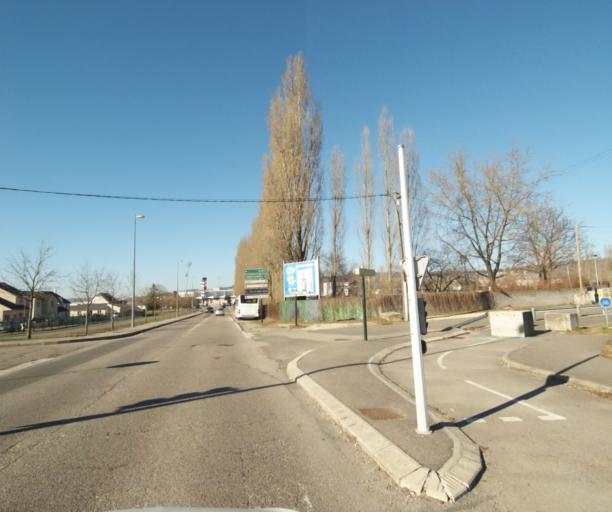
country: FR
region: Lorraine
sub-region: Departement de Meurthe-et-Moselle
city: Tomblaine
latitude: 48.6915
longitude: 6.2138
